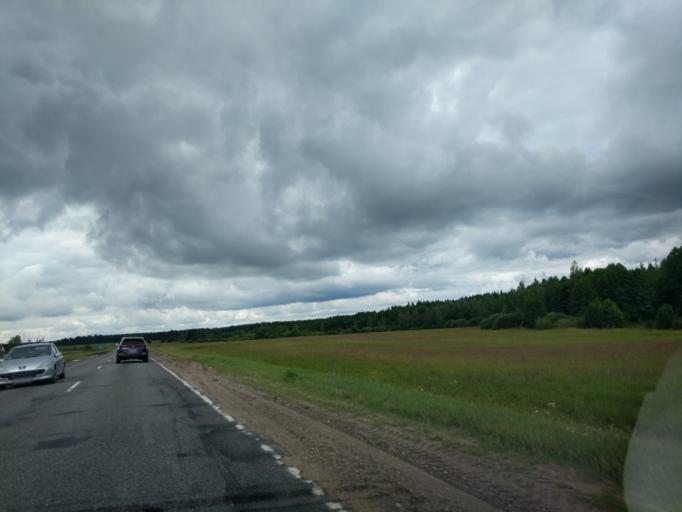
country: BY
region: Minsk
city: Il'ya
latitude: 54.4753
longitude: 27.2641
